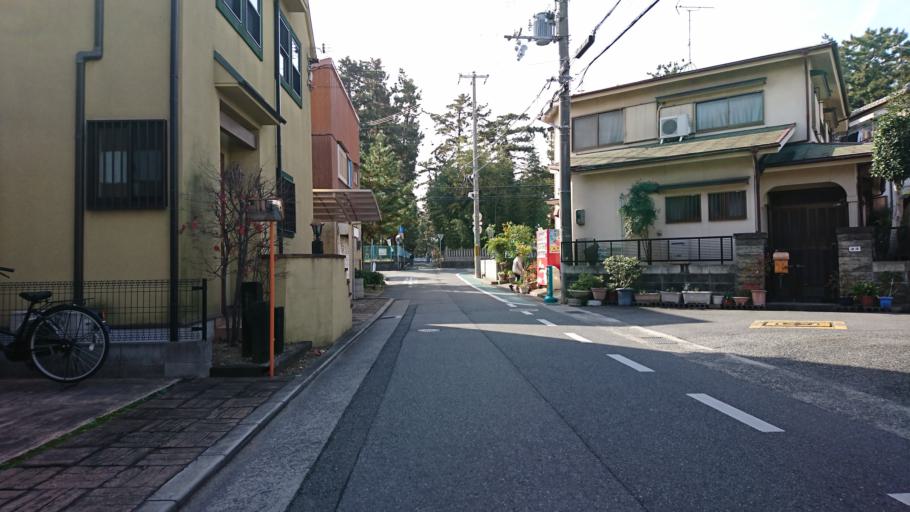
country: JP
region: Hyogo
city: Kakogawacho-honmachi
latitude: 34.7388
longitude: 134.8357
